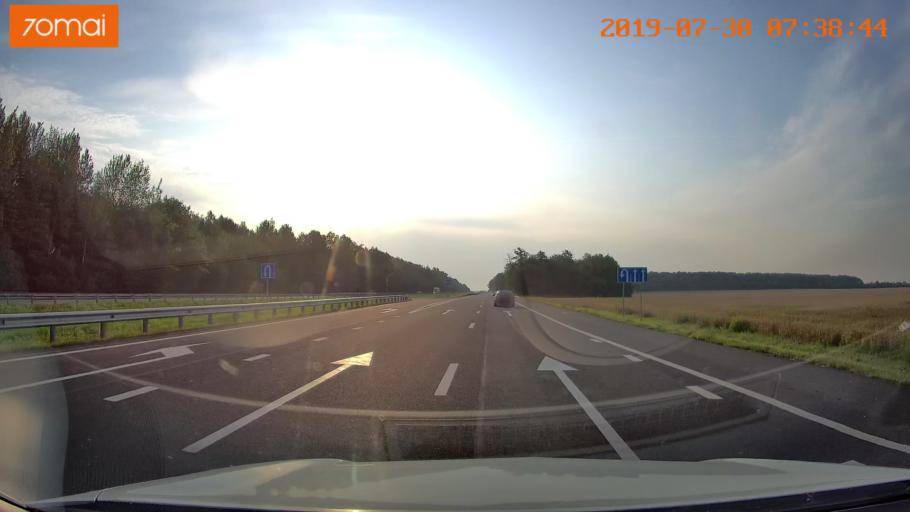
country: RU
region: Kaliningrad
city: Gvardeysk
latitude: 54.6497
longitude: 21.1766
